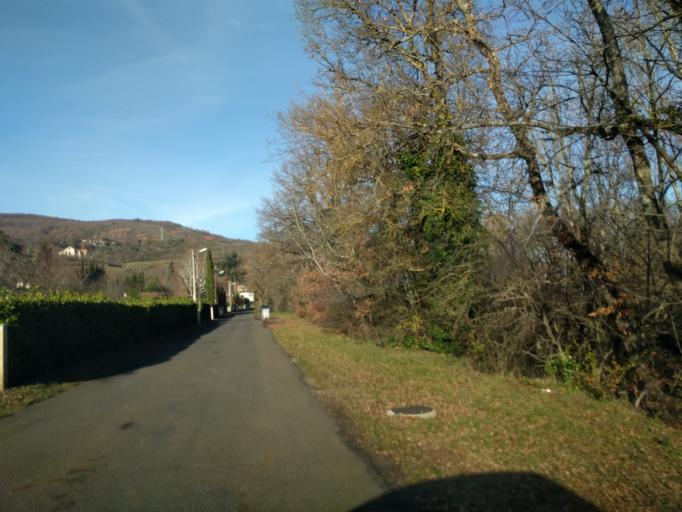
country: FR
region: Languedoc-Roussillon
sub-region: Departement de l'Aude
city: Quillan
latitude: 42.9036
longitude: 2.1876
